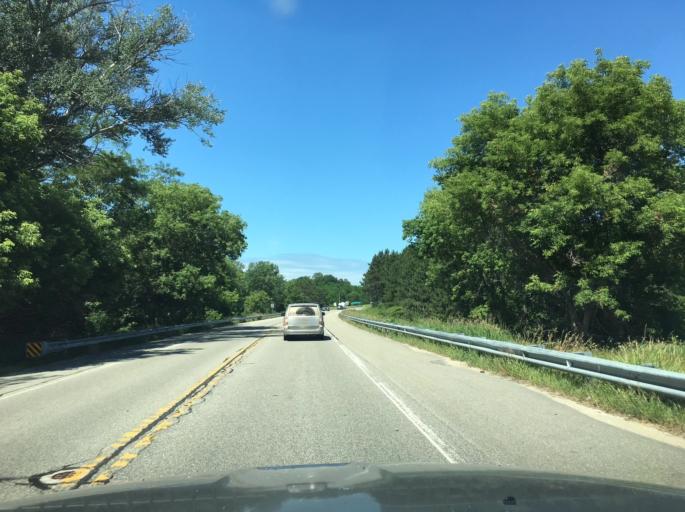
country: US
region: Michigan
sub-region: Osceola County
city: Reed City
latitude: 43.8879
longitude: -85.6376
